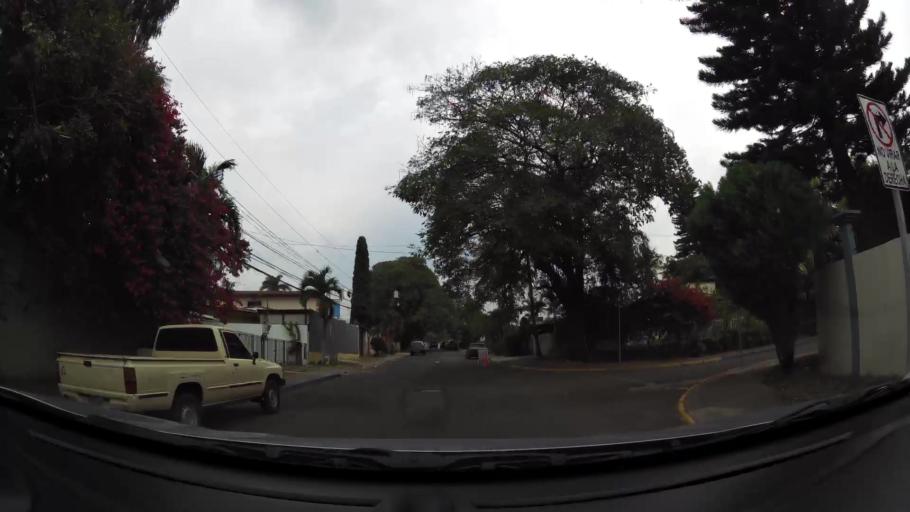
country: HN
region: Francisco Morazan
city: Tegucigalpa
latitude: 14.0831
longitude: -87.1764
